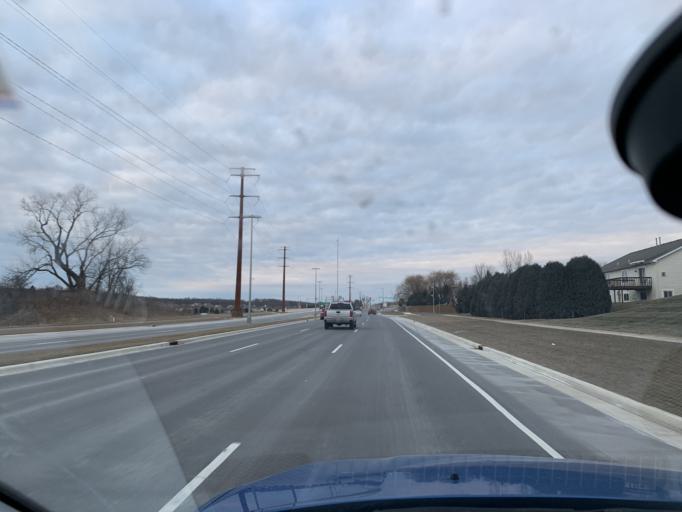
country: US
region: Wisconsin
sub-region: Dane County
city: Verona
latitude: 43.0282
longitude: -89.5331
